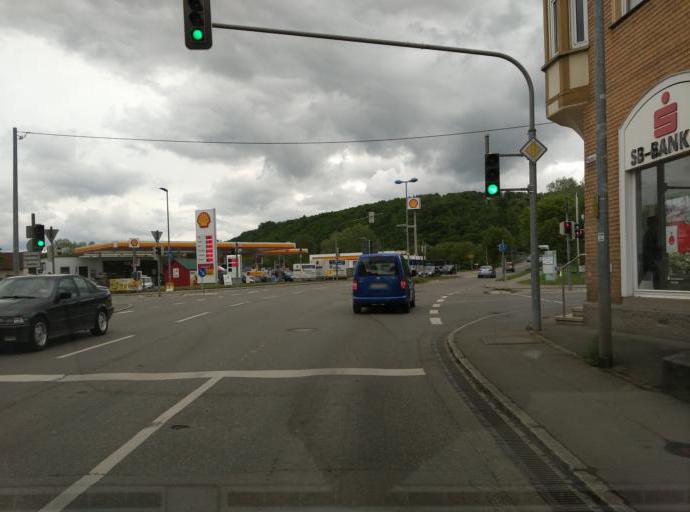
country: DE
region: Baden-Wuerttemberg
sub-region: Tuebingen Region
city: Kirchentellinsfurt
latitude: 48.5314
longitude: 9.1389
